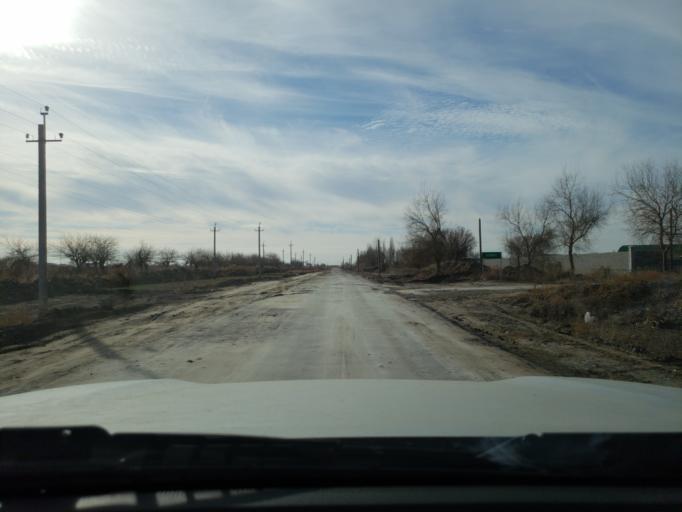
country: TM
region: Dasoguz
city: Dasoguz
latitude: 41.8471
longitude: 59.8786
